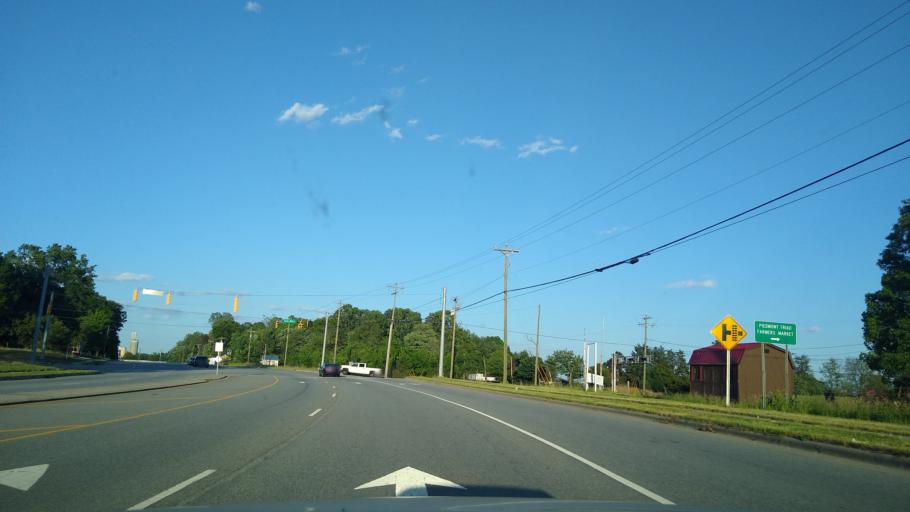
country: US
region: North Carolina
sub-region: Guilford County
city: Oak Ridge
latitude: 36.1021
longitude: -79.9971
